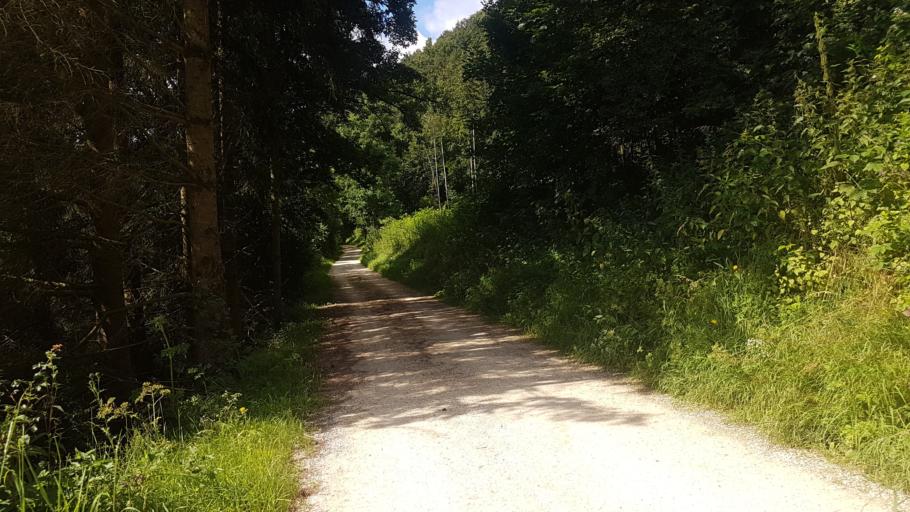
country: DE
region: Bavaria
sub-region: Upper Bavaria
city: Walting
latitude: 48.9456
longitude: 11.3525
